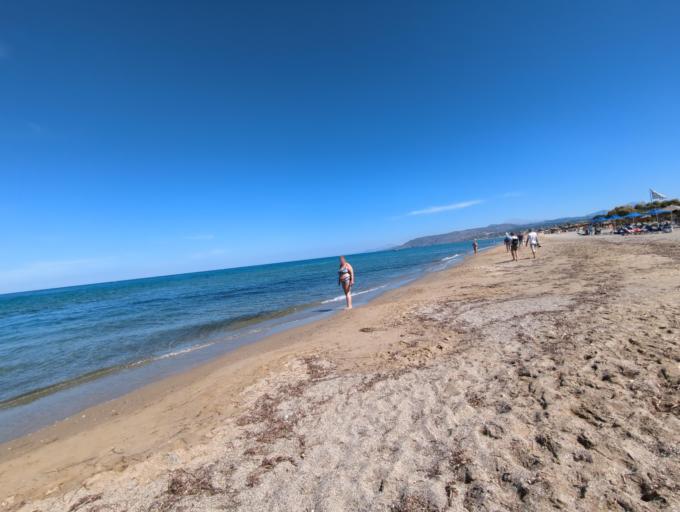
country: GR
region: Crete
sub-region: Nomos Chanias
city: Georgioupolis
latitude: 35.3597
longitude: 24.2677
